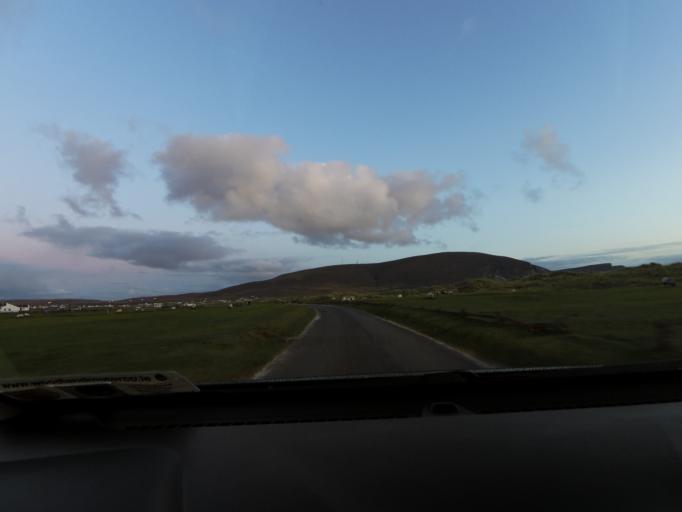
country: IE
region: Connaught
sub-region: Maigh Eo
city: Belmullet
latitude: 53.9741
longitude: -10.0808
